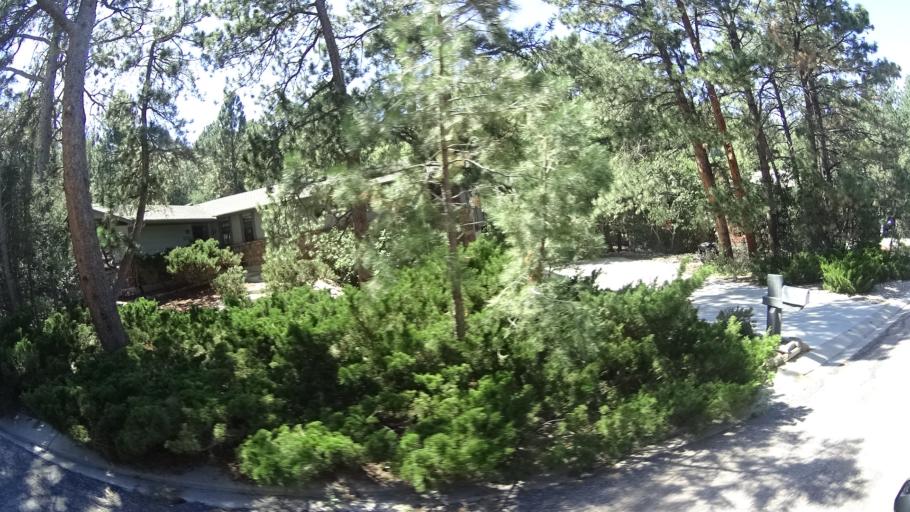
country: US
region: Colorado
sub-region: El Paso County
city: Colorado Springs
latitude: 38.9209
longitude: -104.8029
